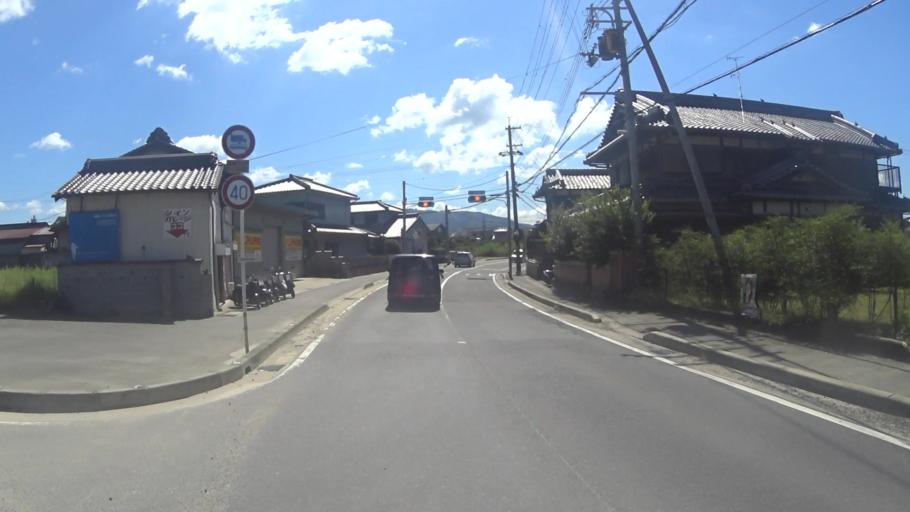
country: JP
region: Kyoto
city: Tanabe
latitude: 34.8378
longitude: 135.7967
